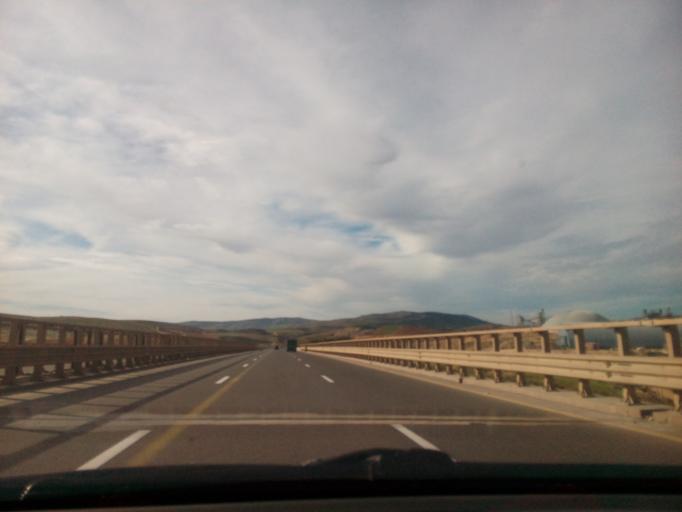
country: DZ
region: Sidi Bel Abbes
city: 'Ain el Berd
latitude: 35.4604
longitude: -0.3852
